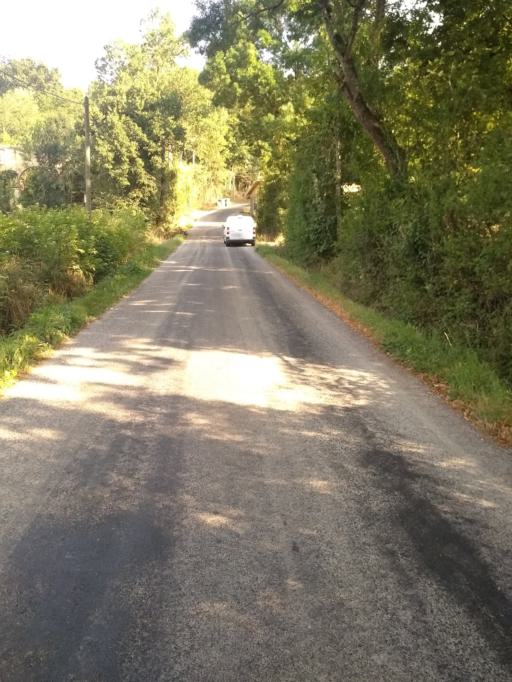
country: FR
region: Midi-Pyrenees
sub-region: Departement de la Haute-Garonne
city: Montaigut-sur-Save
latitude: 43.6870
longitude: 1.2242
